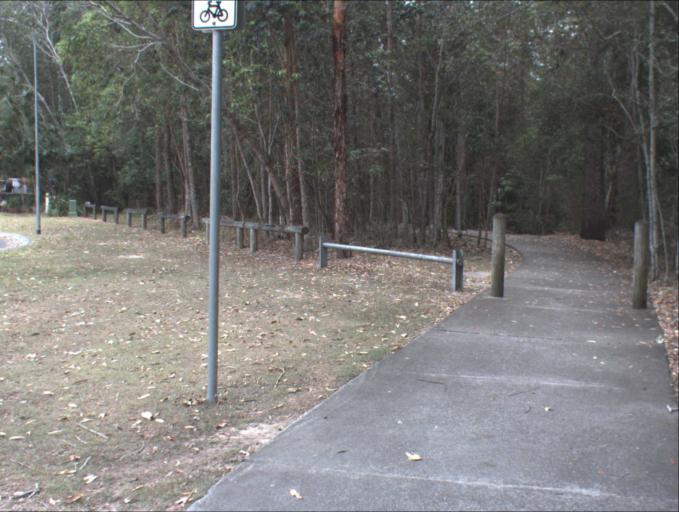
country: AU
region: Queensland
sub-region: Logan
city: Beenleigh
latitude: -27.6579
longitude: 153.2076
